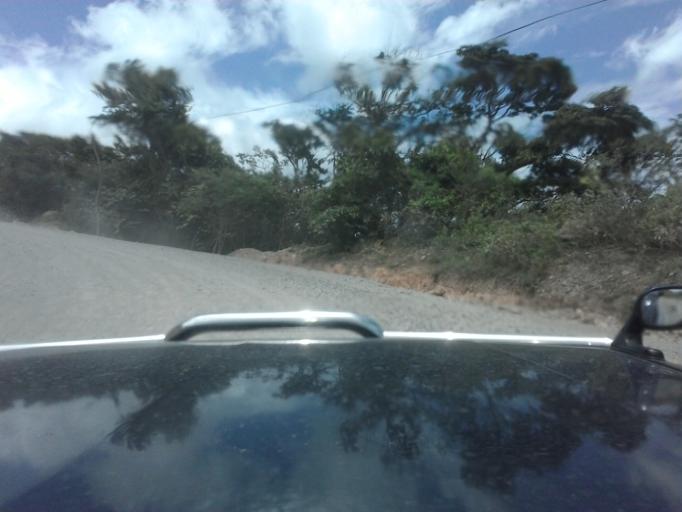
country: CR
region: Guanacaste
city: Juntas
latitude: 10.2611
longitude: -84.8391
